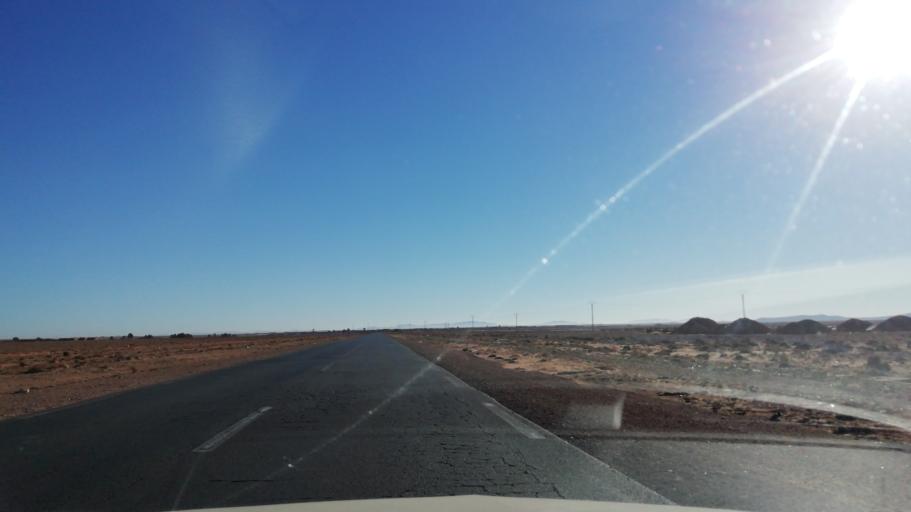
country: DZ
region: El Bayadh
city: El Bayadh
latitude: 33.8550
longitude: 0.6024
